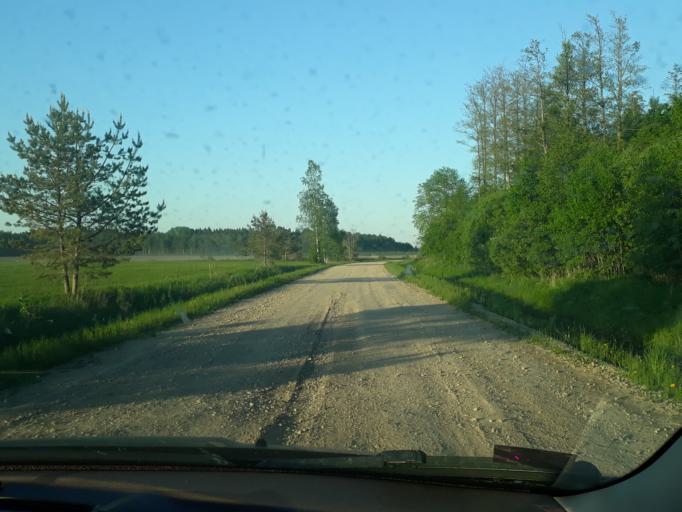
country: EE
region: Paernumaa
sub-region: Tootsi vald
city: Tootsi
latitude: 58.5803
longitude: 24.9229
